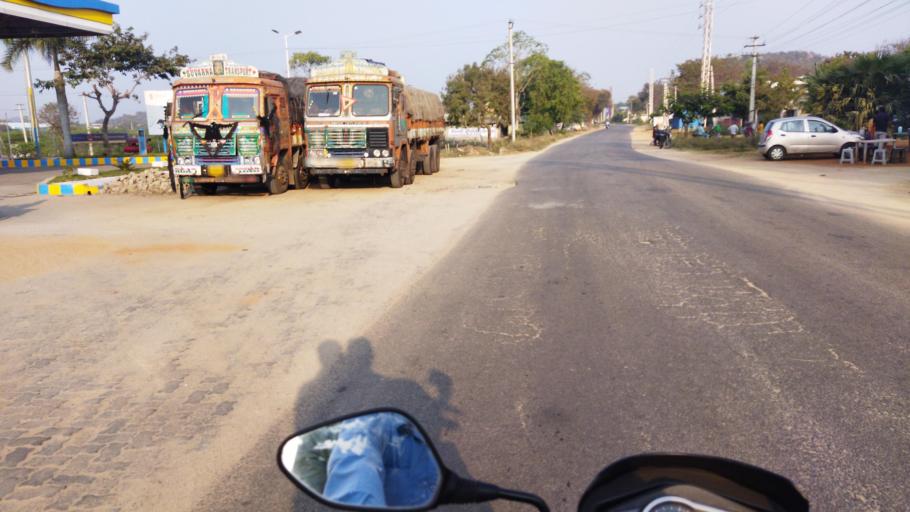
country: IN
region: Telangana
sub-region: Nalgonda
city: Nalgonda
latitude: 17.2365
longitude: 79.1209
